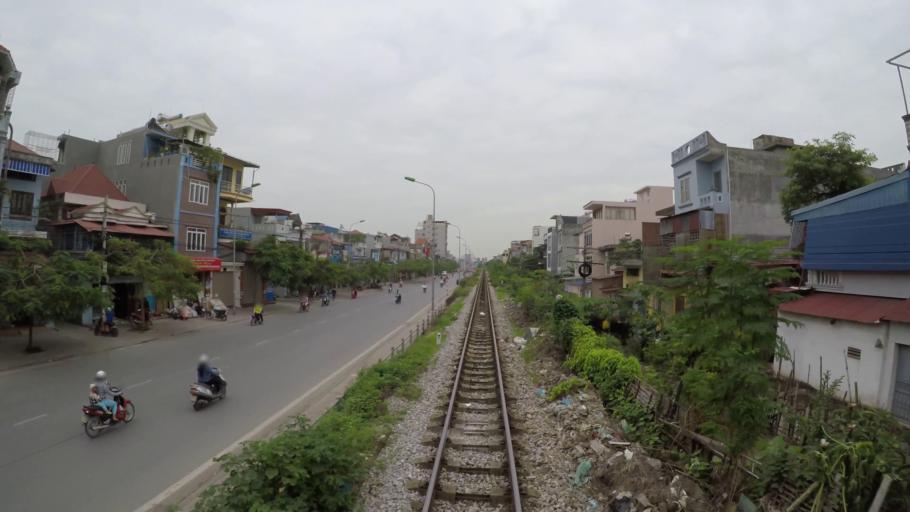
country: VN
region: Hai Phong
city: An Duong
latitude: 20.8737
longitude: 106.6430
